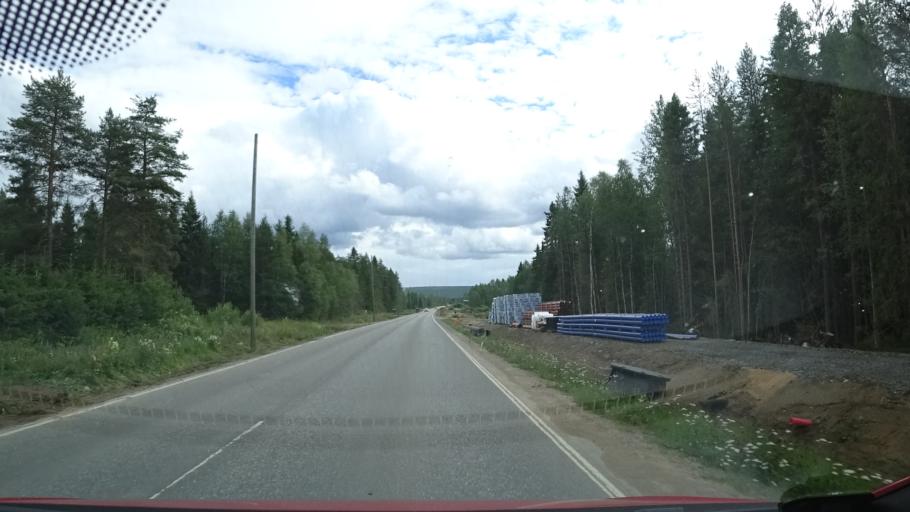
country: FI
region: Lapland
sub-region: Rovaniemi
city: Rovaniemi
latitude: 66.5325
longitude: 25.7342
